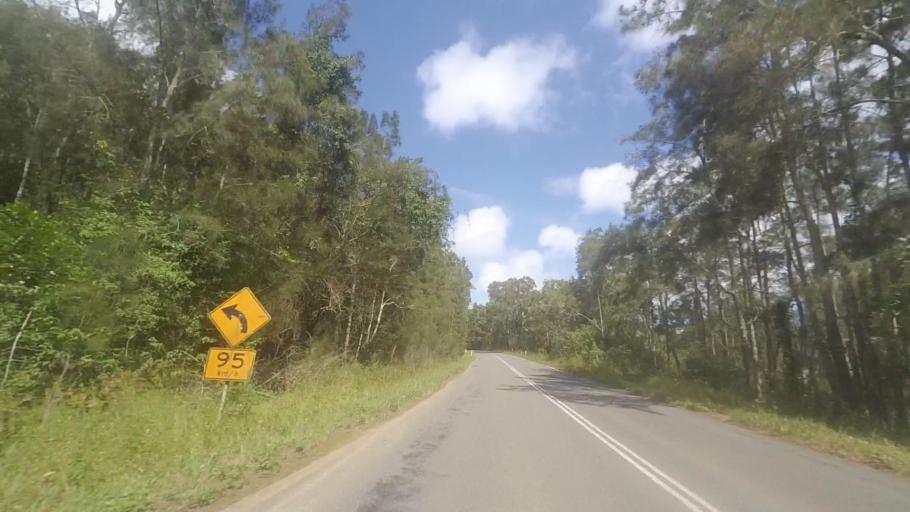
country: AU
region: New South Wales
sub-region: Great Lakes
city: Bulahdelah
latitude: -32.3909
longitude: 152.4310
